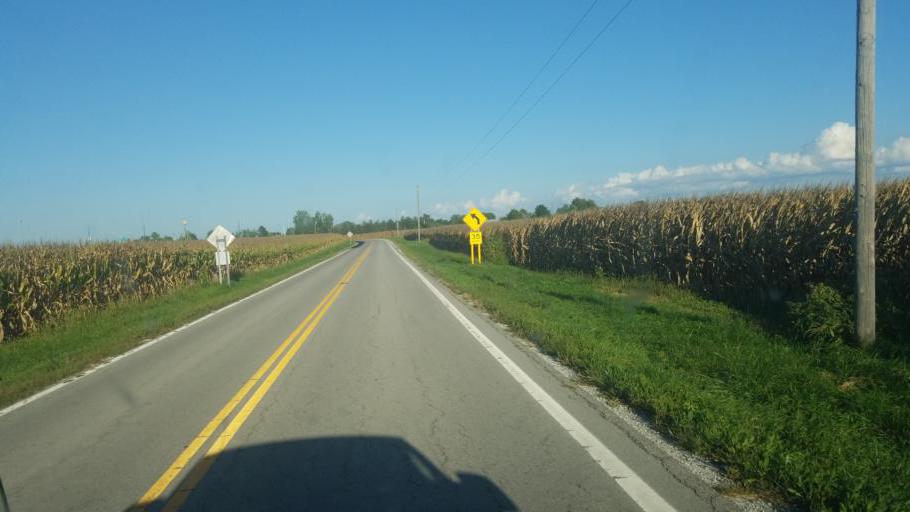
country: US
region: Ohio
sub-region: Wyandot County
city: Carey
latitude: 40.9378
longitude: -83.4082
